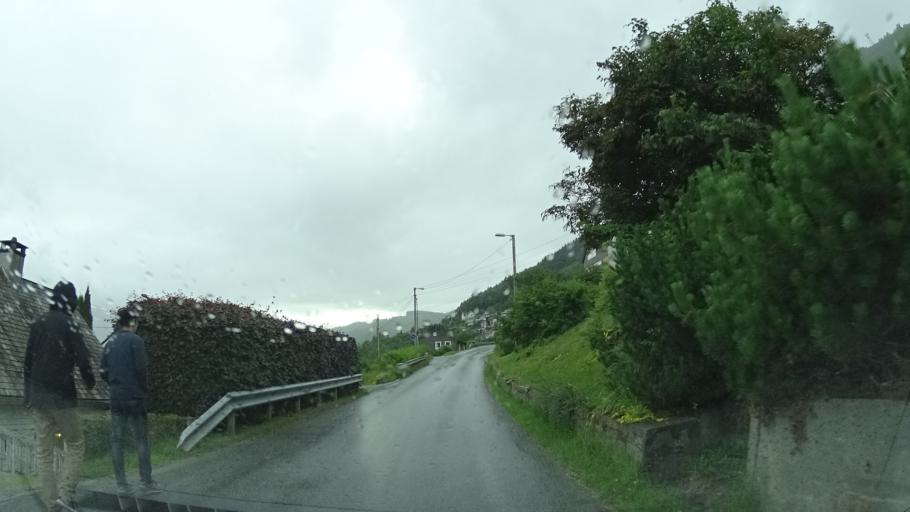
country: NO
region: Hordaland
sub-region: Voss
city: Voss
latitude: 60.6311
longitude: 6.4112
